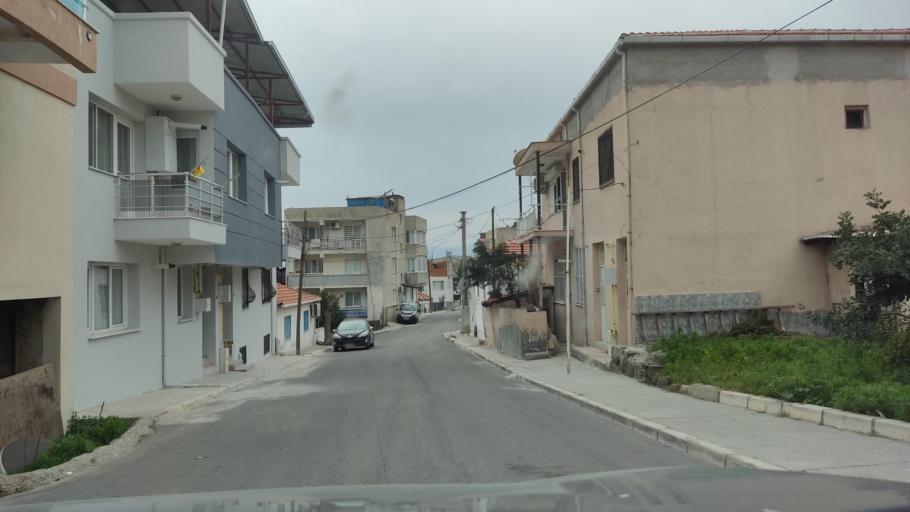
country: TR
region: Izmir
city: Karsiyaka
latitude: 38.5015
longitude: 27.0777
